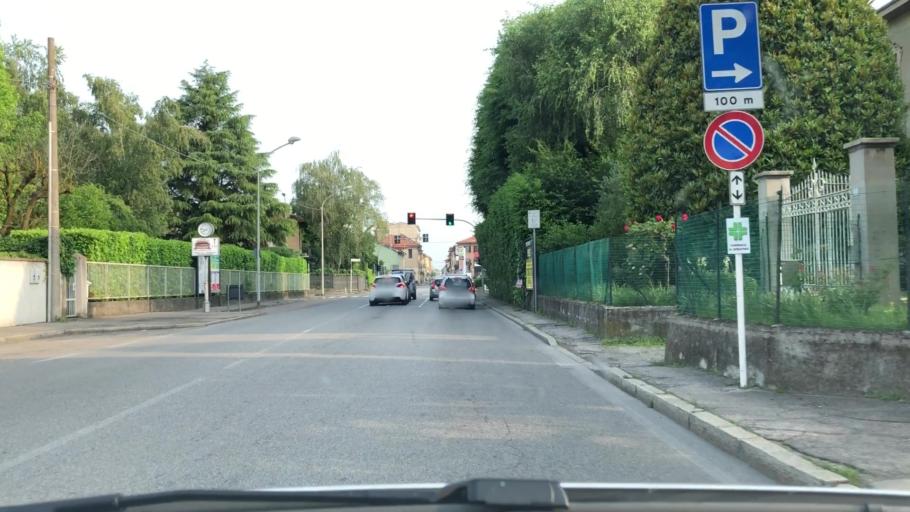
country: IT
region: Lombardy
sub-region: Provincia di Monza e Brianza
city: Barlassina
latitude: 45.6536
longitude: 9.1307
